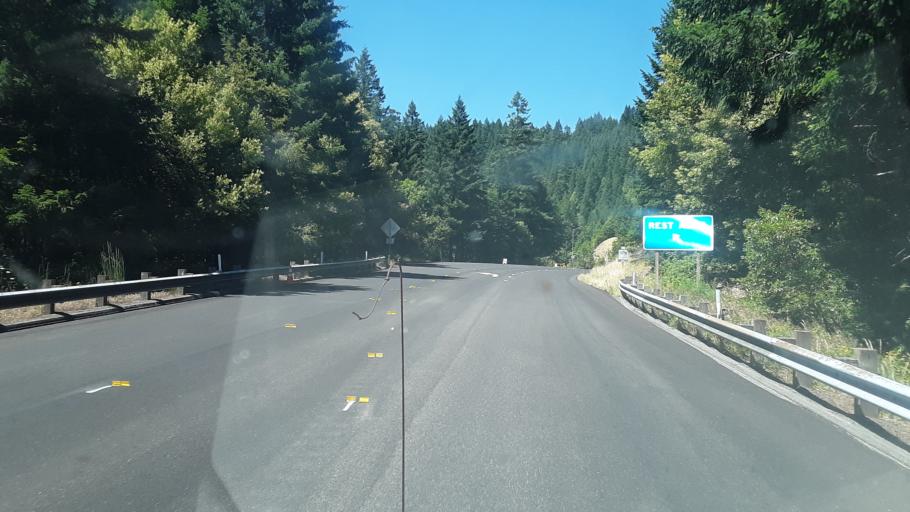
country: US
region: Oregon
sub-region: Josephine County
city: Cave Junction
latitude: 41.9652
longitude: -123.7471
